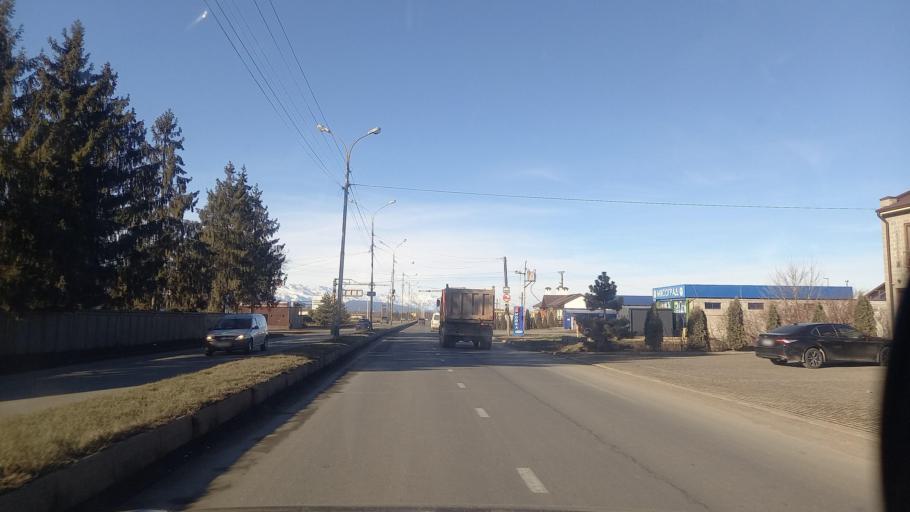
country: RU
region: North Ossetia
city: Vladikavkaz
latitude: 43.0254
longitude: 44.6366
